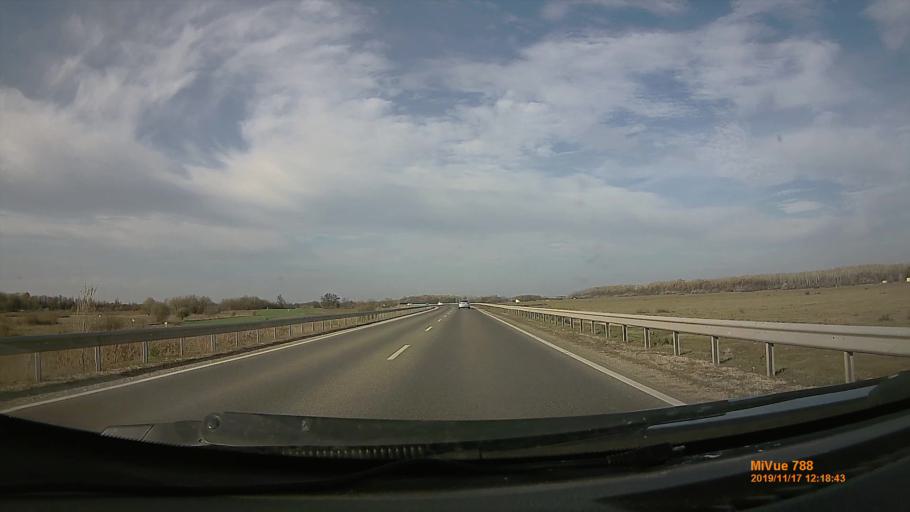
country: HU
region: Bacs-Kiskun
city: Kecskemet
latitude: 46.9221
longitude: 19.7232
